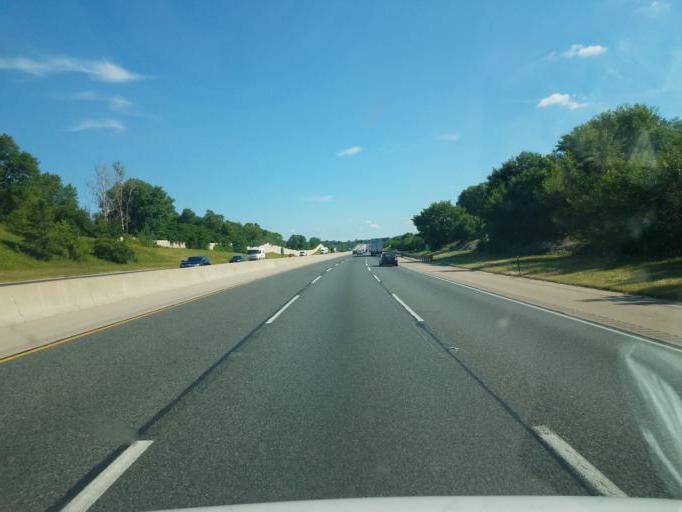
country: US
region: Illinois
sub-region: Winnebago County
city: Roscoe
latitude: 42.4251
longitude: -88.9858
